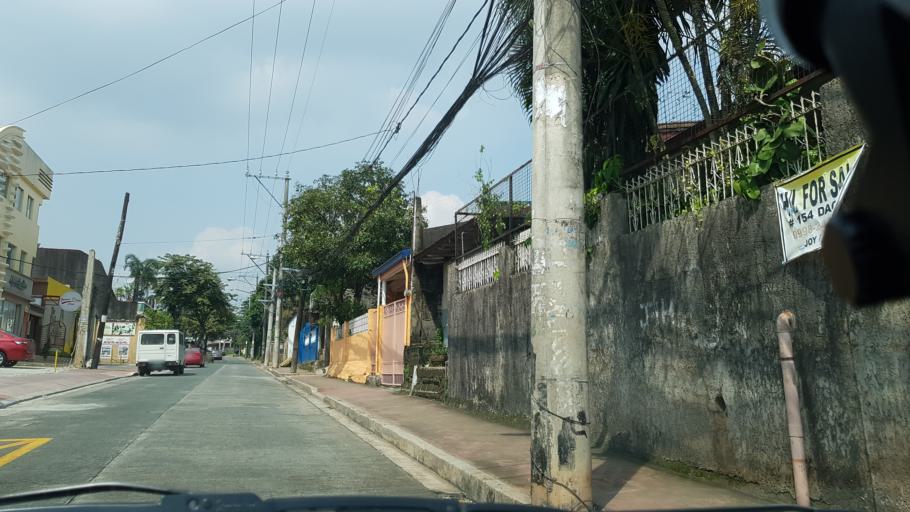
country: PH
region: Calabarzon
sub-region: Province of Rizal
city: Antipolo
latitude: 14.6501
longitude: 121.1195
